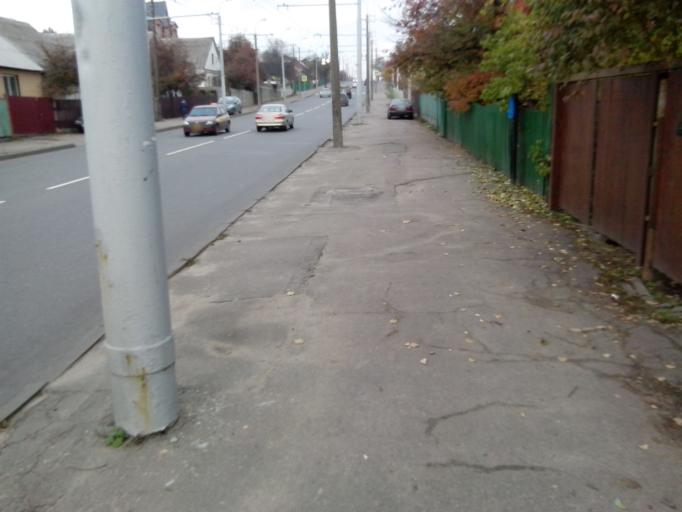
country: BY
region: Minsk
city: Minsk
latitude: 53.9441
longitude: 27.5903
